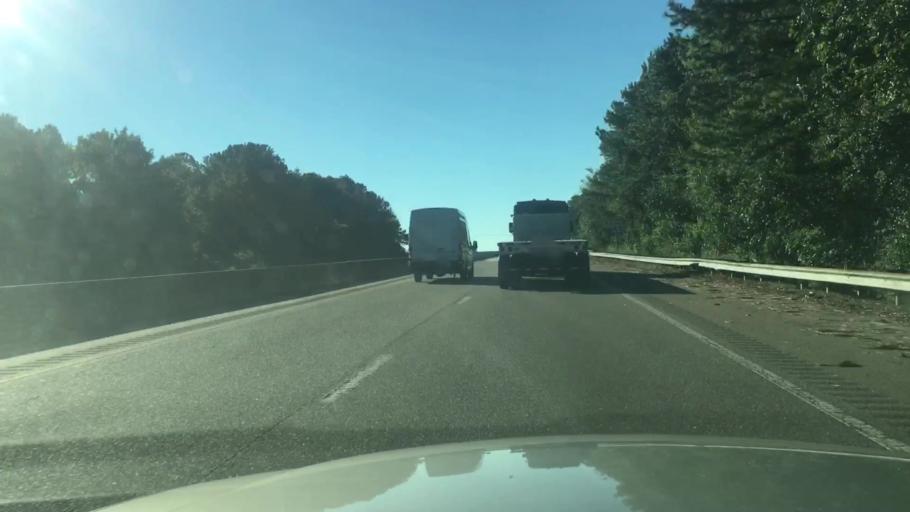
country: US
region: North Carolina
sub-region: Cumberland County
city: Fayetteville
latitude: 35.0470
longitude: -78.9409
